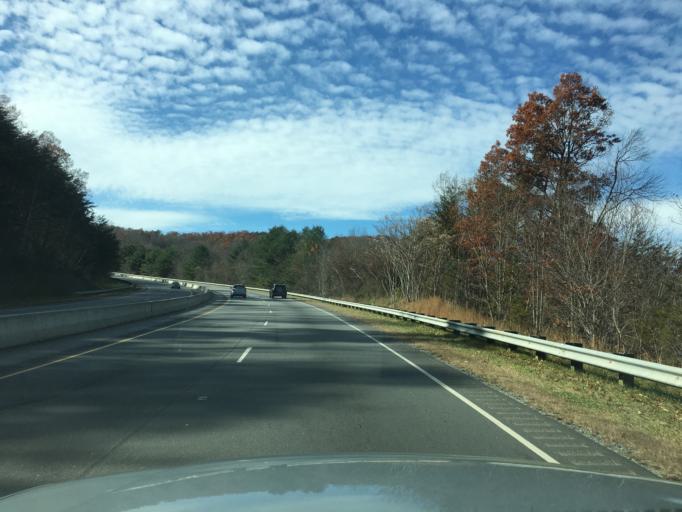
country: US
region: North Carolina
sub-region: McDowell County
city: Marion
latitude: 35.6695
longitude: -81.9925
